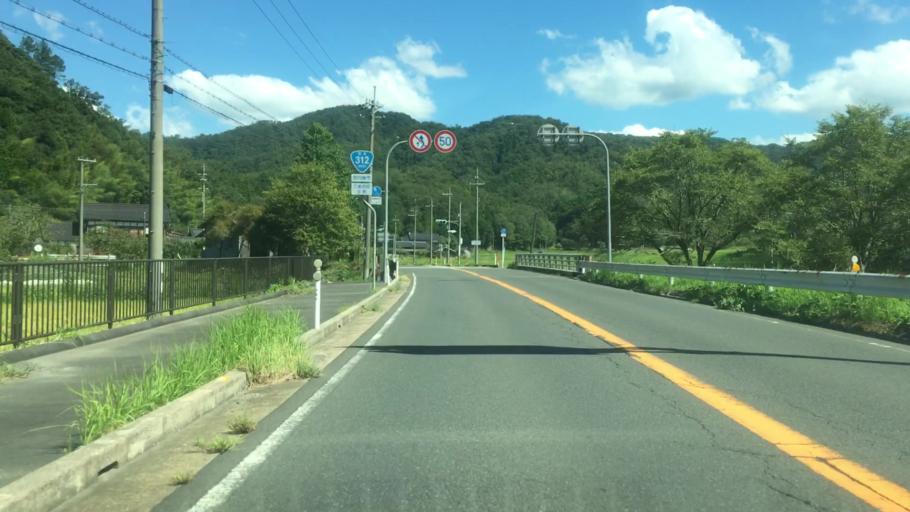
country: JP
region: Hyogo
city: Toyooka
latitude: 35.5734
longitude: 134.9793
